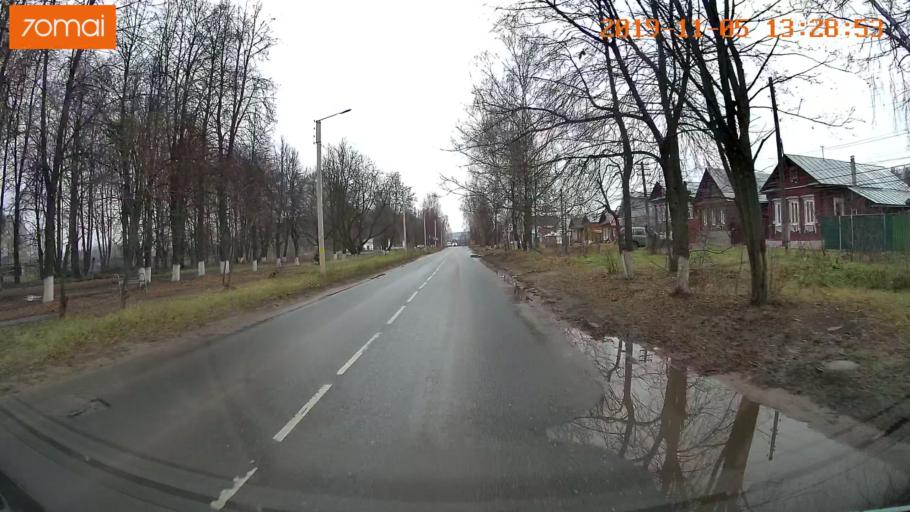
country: RU
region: Ivanovo
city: Shuya
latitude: 56.8572
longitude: 41.3928
